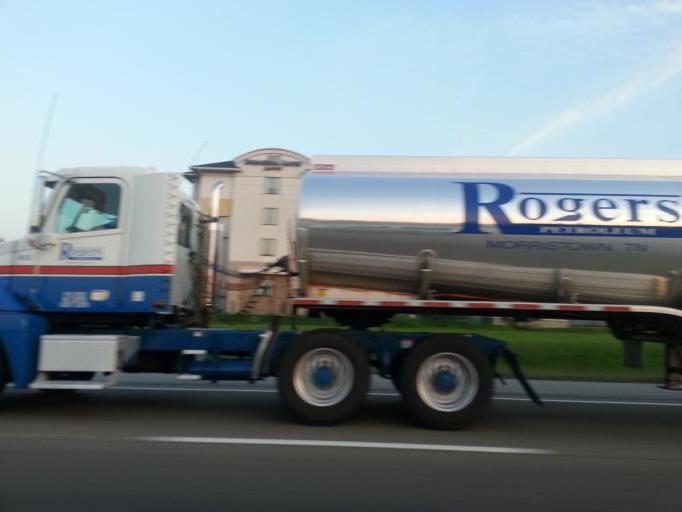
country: US
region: Tennessee
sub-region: Knox County
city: Farragut
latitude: 35.9046
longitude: -84.1510
